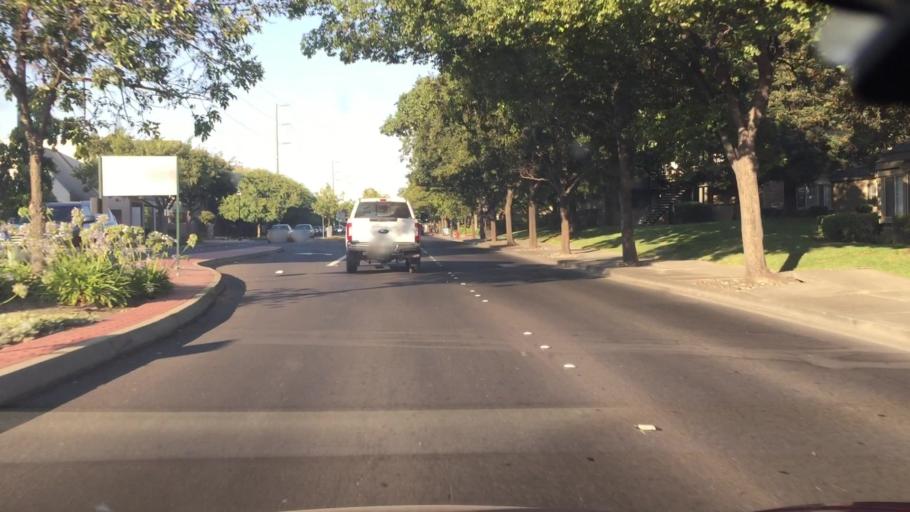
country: US
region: California
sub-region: Alameda County
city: Livermore
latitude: 37.6815
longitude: -121.7757
